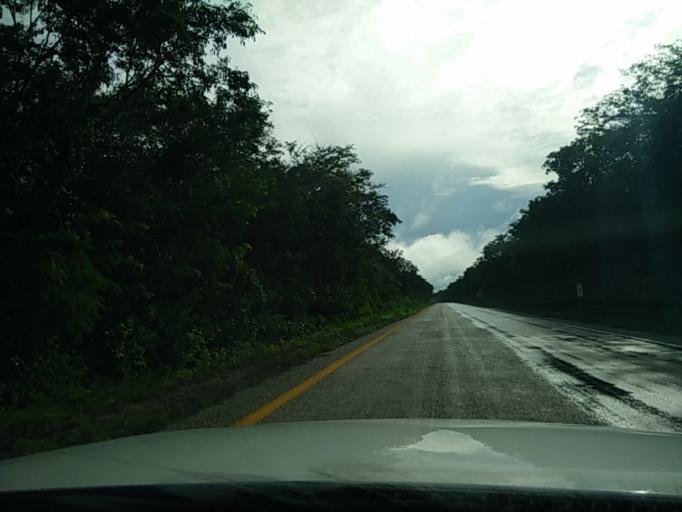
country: MX
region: Yucatan
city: Tunkas
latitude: 20.7621
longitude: -88.7854
